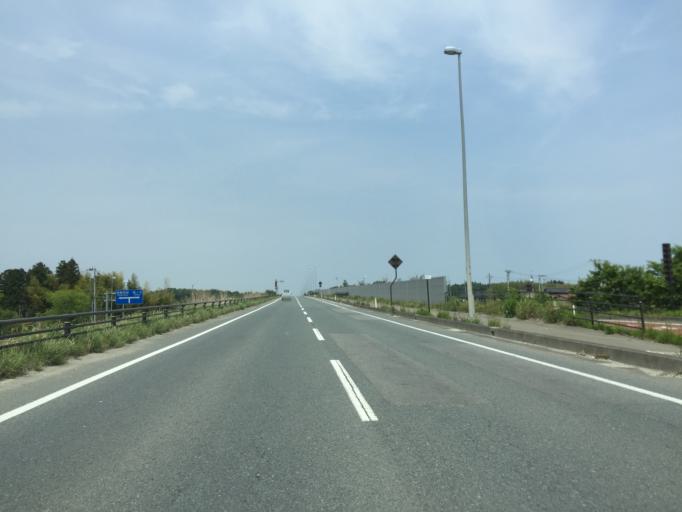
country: JP
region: Miyagi
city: Marumori
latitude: 37.8000
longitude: 140.9437
